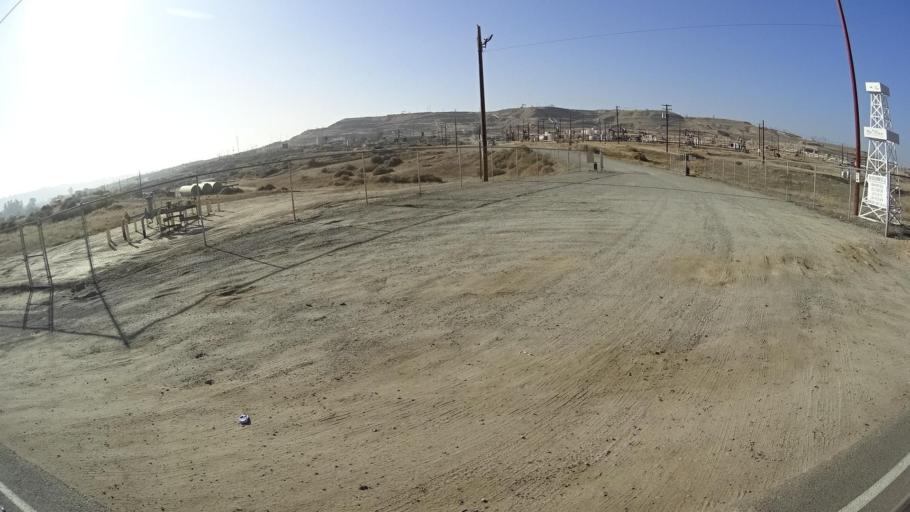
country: US
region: California
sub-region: Kern County
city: Oildale
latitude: 35.4378
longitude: -118.9453
